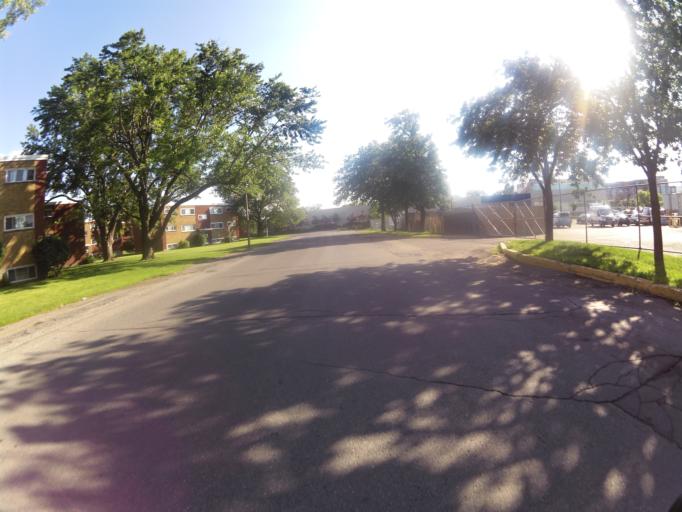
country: CA
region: Ontario
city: Ottawa
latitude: 45.3809
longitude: -75.7402
